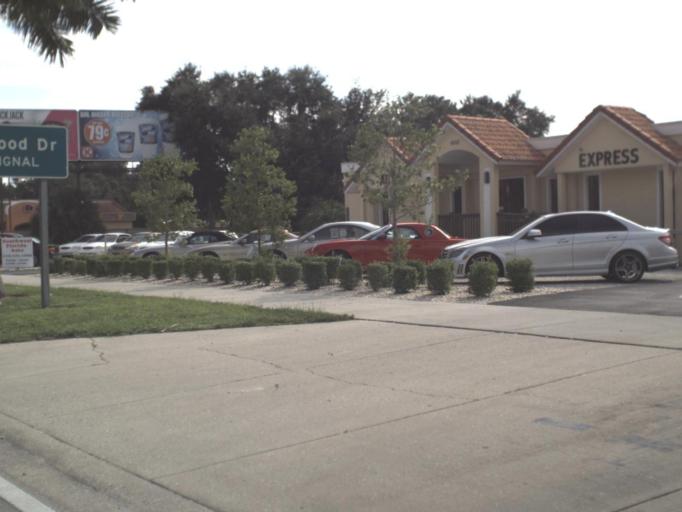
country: US
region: Florida
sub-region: Lee County
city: Tice
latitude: 26.6788
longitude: -81.8078
